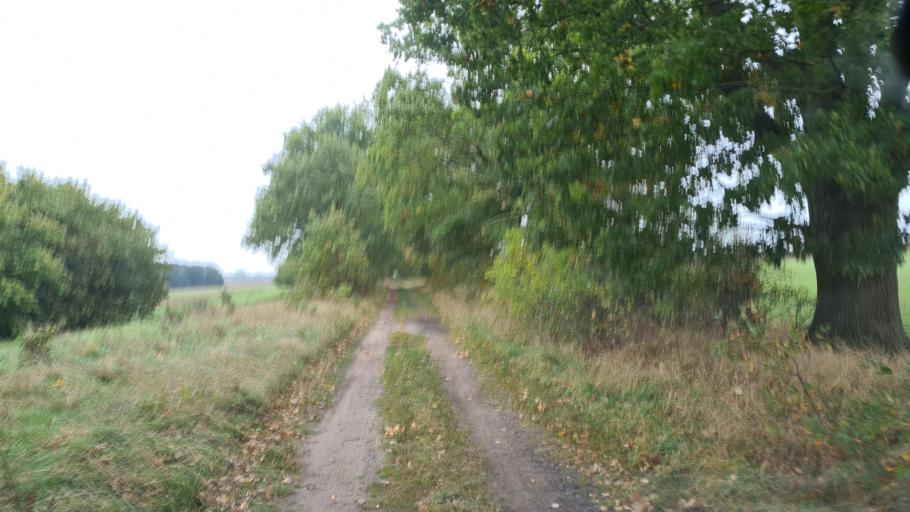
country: DE
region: Brandenburg
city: Furstenwalde
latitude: 52.4189
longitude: 14.0280
